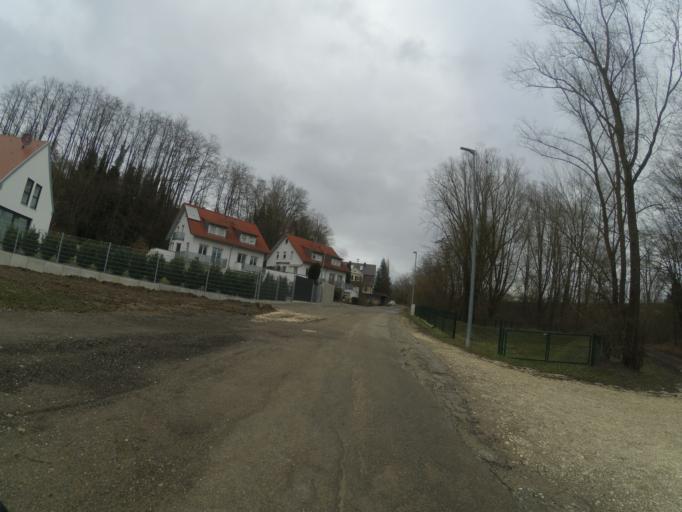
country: DE
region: Bavaria
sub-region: Swabia
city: Senden
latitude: 48.3146
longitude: 10.0616
